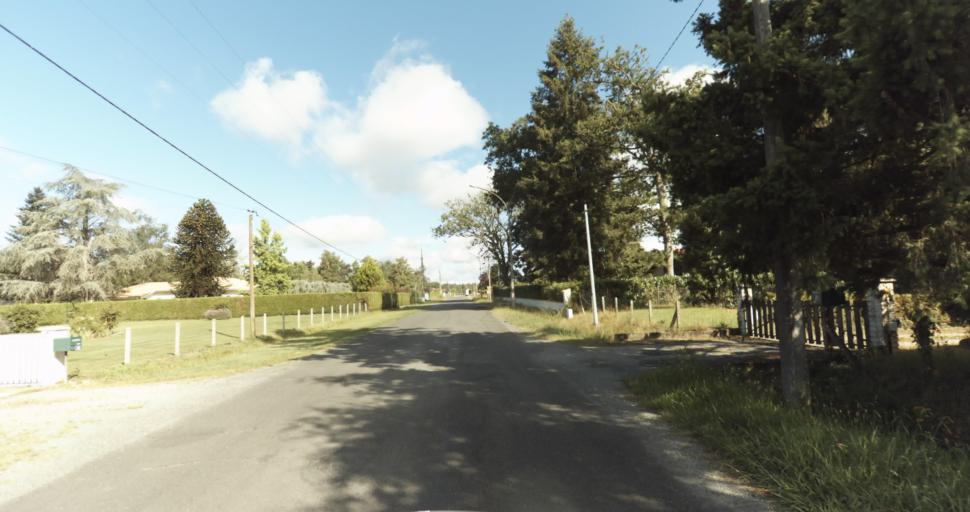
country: FR
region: Aquitaine
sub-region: Departement de la Gironde
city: Bazas
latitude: 44.4406
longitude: -0.2428
